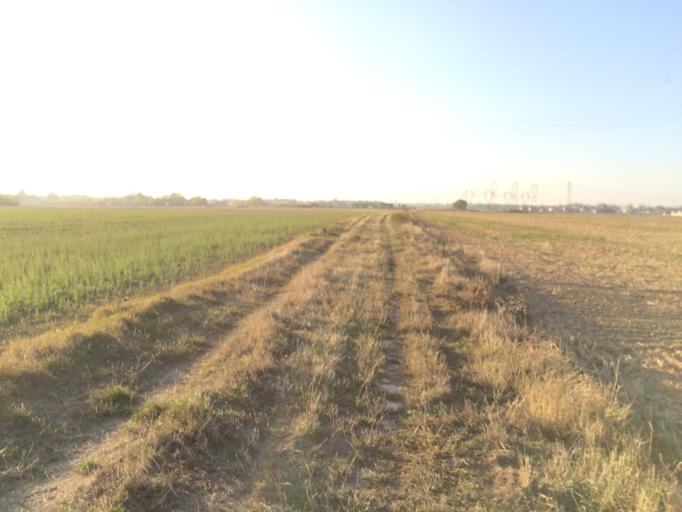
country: FR
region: Ile-de-France
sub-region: Departement de l'Essonne
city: Nozay
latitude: 48.6629
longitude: 2.2255
